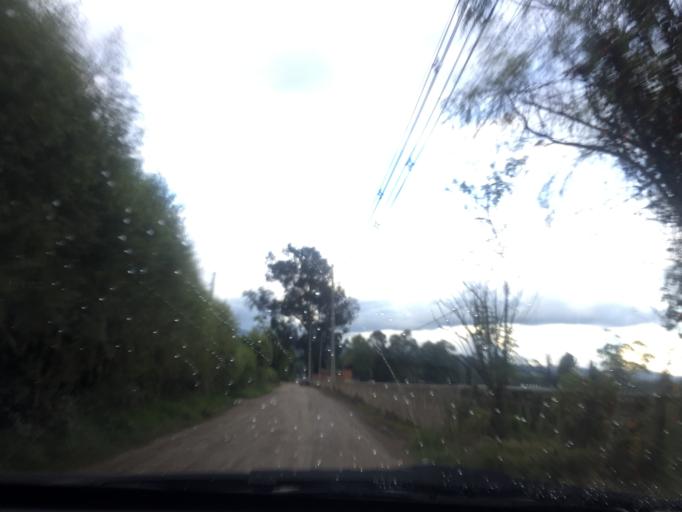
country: CO
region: Cundinamarca
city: Cogua
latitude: 5.0649
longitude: -73.9312
